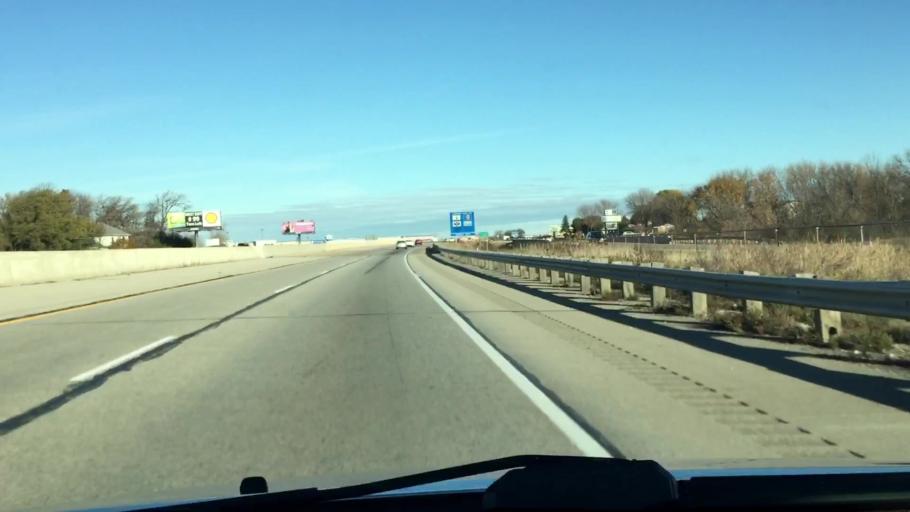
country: US
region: Wisconsin
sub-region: Fond du Lac County
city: Fond du Lac
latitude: 43.7662
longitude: -88.4803
